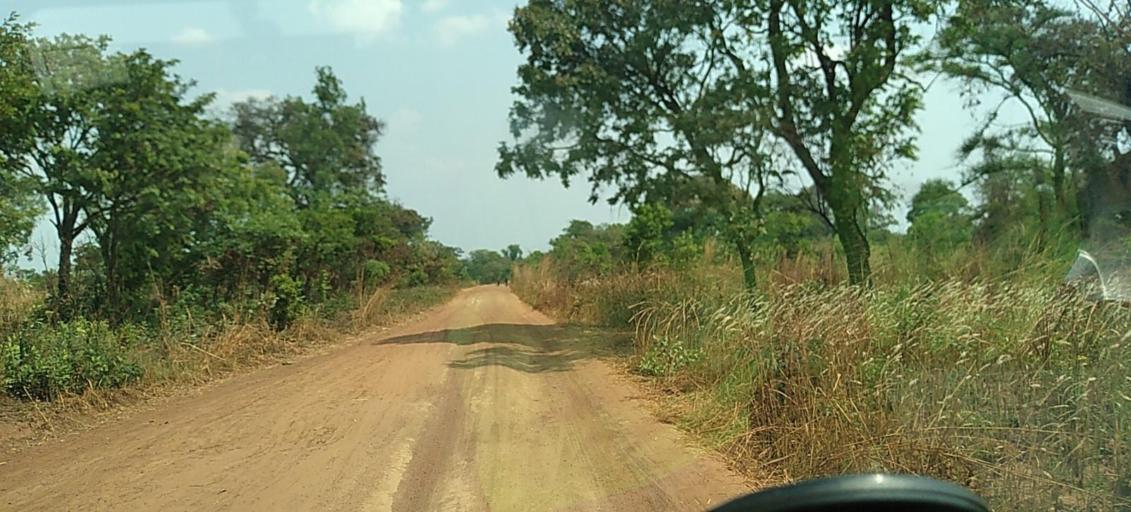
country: ZM
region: North-Western
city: Kansanshi
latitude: -12.1056
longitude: 26.3657
